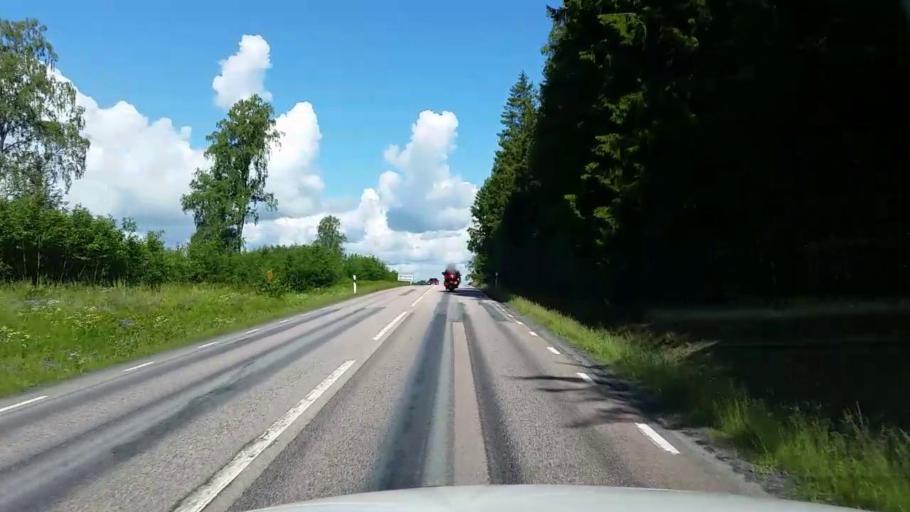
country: SE
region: Vaestmanland
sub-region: Kopings Kommun
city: Kolsva
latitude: 59.6158
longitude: 15.8244
